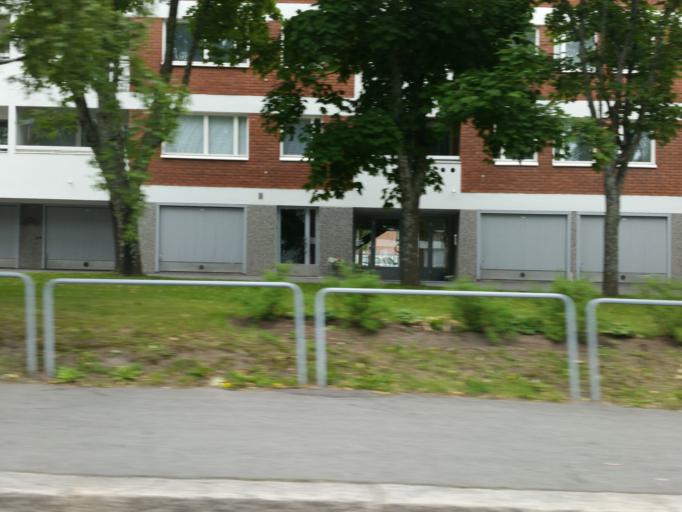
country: FI
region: Northern Savo
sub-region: Kuopio
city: Kuopio
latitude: 62.8896
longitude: 27.6932
